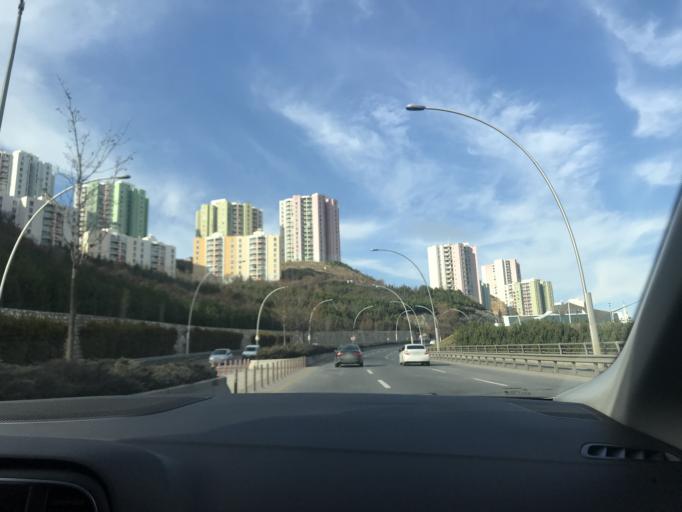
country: TR
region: Ankara
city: Mamak
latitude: 39.9965
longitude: 32.8963
